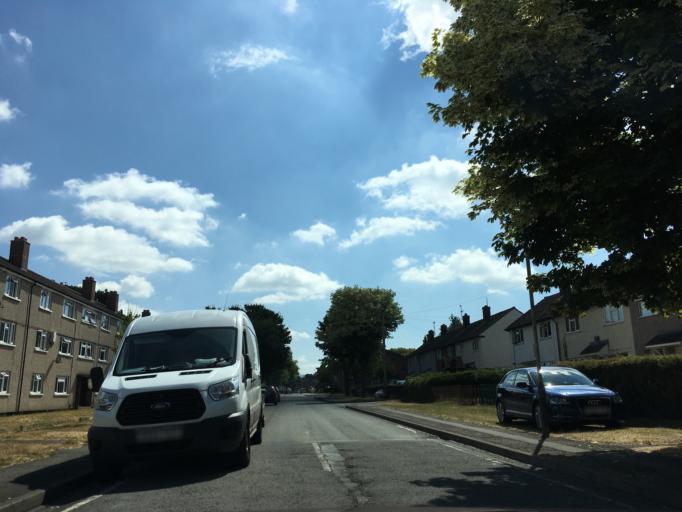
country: GB
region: England
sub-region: Gloucestershire
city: Uckington
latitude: 51.9040
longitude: -2.1190
